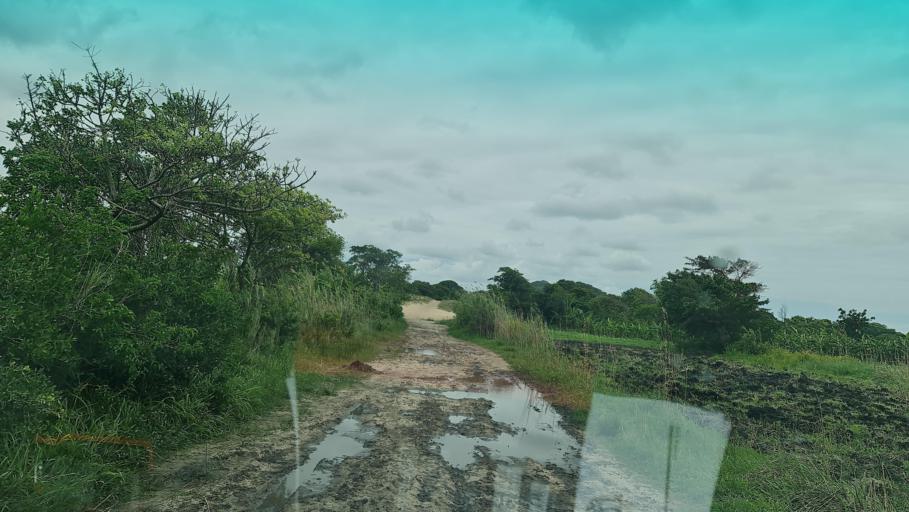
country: MZ
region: Maputo City
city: Maputo
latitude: -25.6988
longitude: 32.7054
